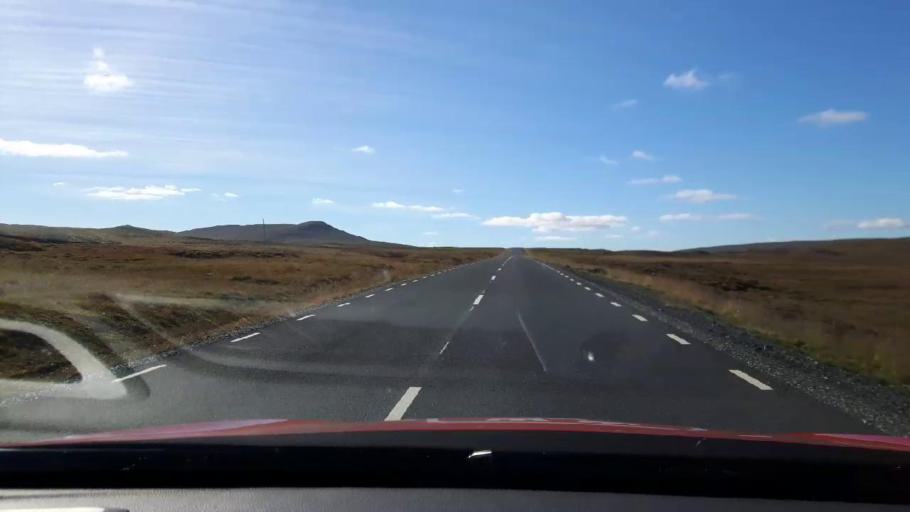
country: NO
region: Nordland
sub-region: Hattfjelldal
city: Hattfjelldal
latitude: 65.0702
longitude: 14.3945
